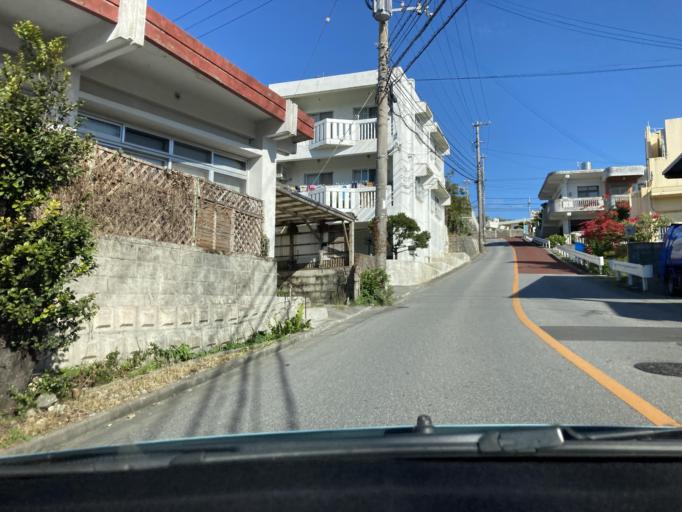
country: JP
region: Okinawa
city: Chatan
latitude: 26.3017
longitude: 127.7972
